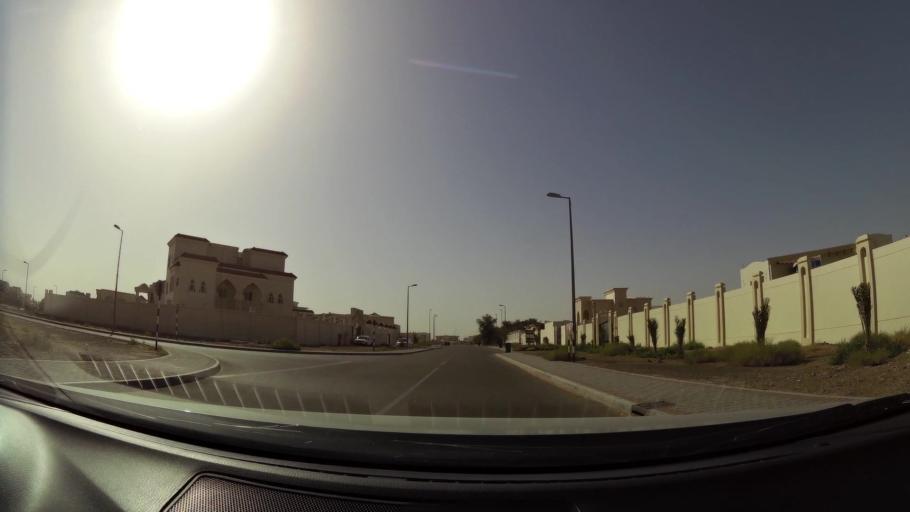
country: OM
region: Al Buraimi
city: Al Buraymi
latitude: 24.3554
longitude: 55.7927
